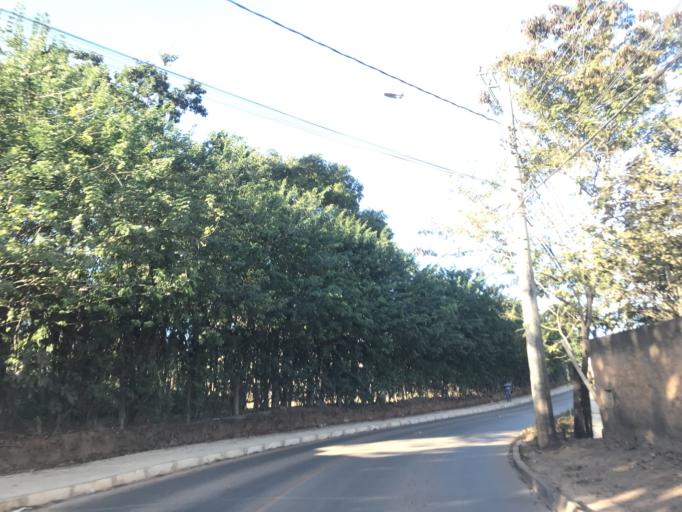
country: BR
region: Federal District
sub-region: Brasilia
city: Brasilia
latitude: -15.8837
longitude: -47.7714
